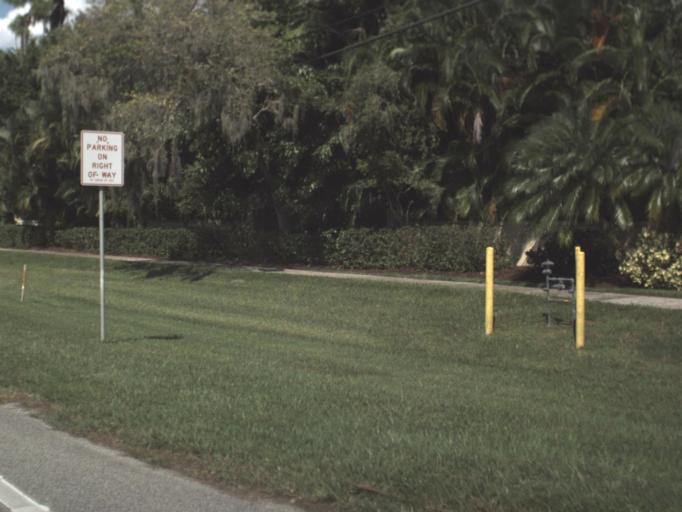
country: US
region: Florida
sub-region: Sarasota County
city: Osprey
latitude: 27.2089
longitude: -82.4902
